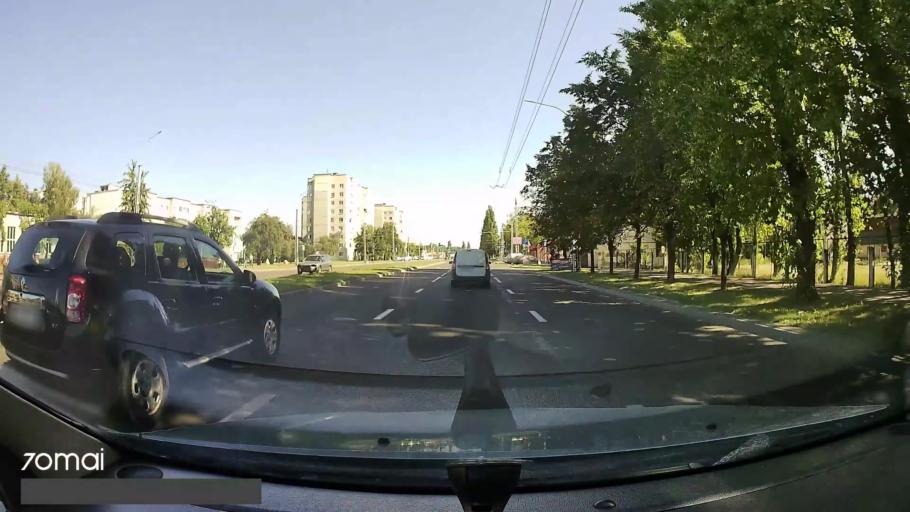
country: BY
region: Brest
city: Brest
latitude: 52.1051
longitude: 23.7393
